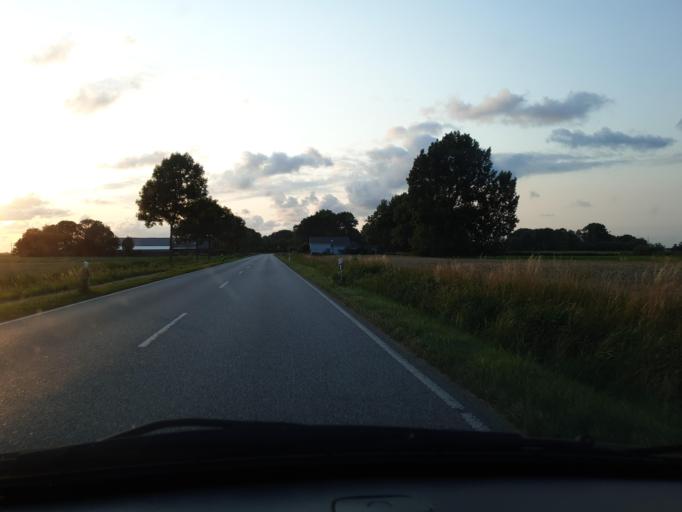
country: DE
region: Schleswig-Holstein
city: Schmedeswurth
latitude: 53.9284
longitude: 9.0376
